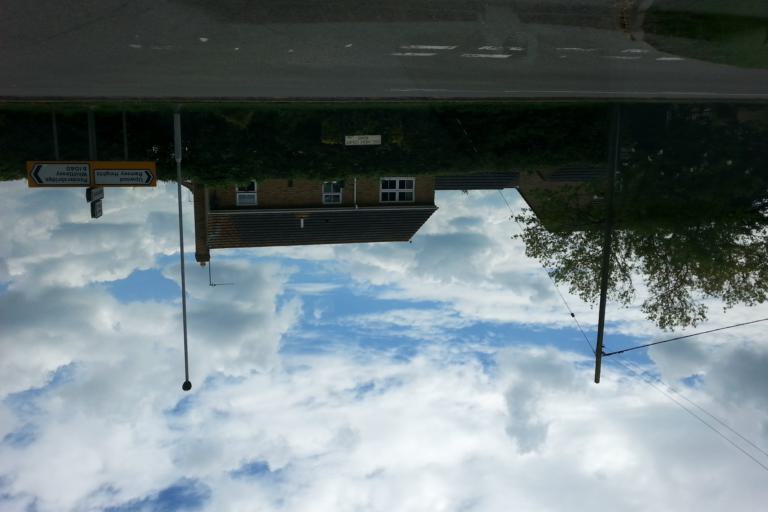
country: GB
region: England
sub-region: Cambridgeshire
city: Ramsey
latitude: 52.4692
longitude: -0.1535
